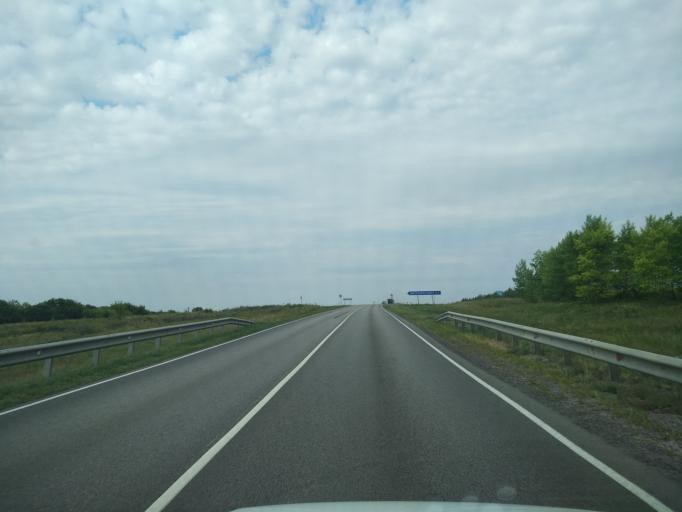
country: RU
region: Voronezj
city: Pereleshinskiy
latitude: 51.8535
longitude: 40.3314
